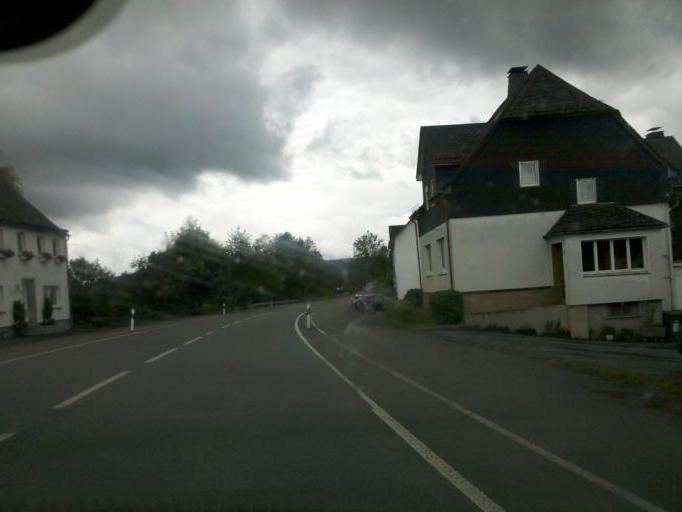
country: DE
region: North Rhine-Westphalia
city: Eslohe
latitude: 51.2591
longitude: 8.2295
